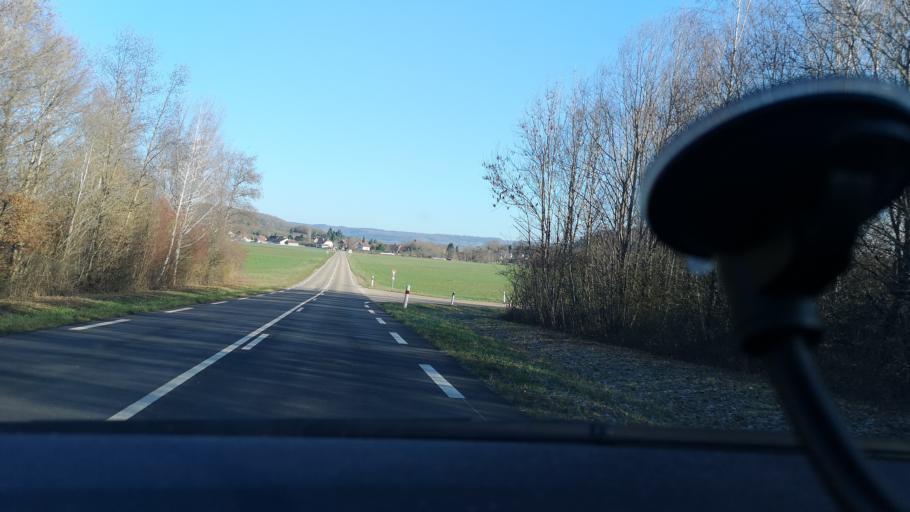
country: FR
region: Franche-Comte
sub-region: Departement du Jura
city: Bletterans
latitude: 46.7592
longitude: 5.5111
